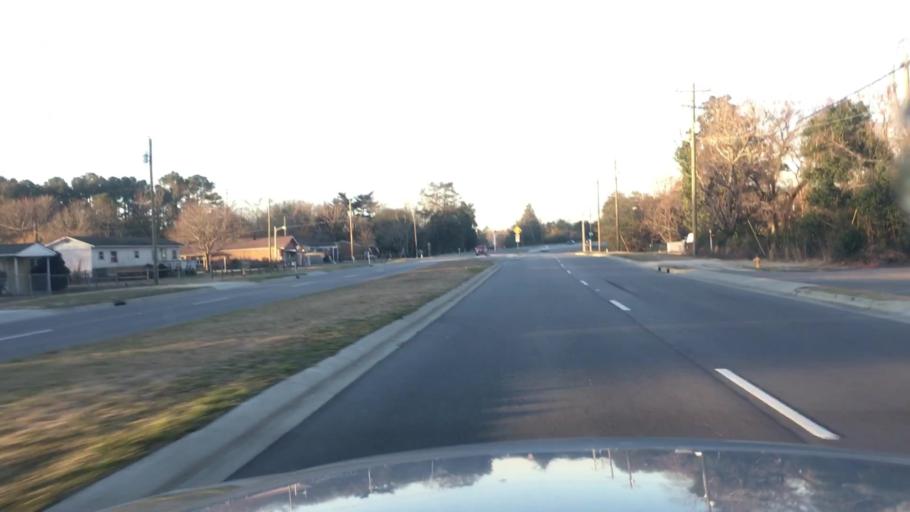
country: US
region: North Carolina
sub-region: Cumberland County
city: Hope Mills
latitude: 35.0003
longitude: -78.9290
